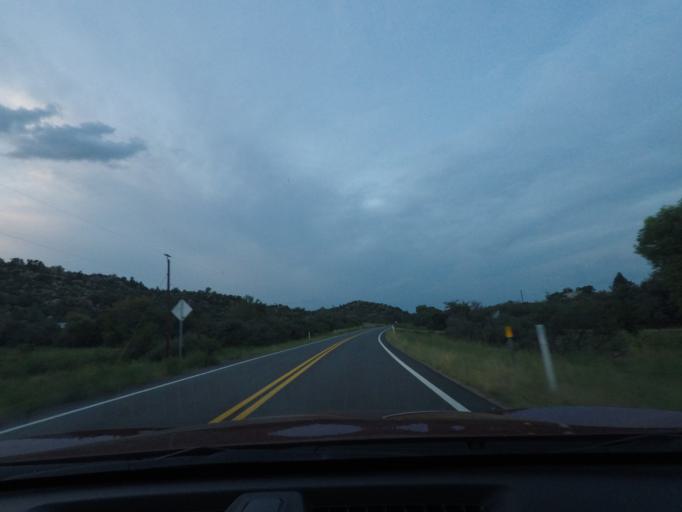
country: US
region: Arizona
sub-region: Yavapai County
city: Prescott
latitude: 34.5084
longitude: -112.6913
